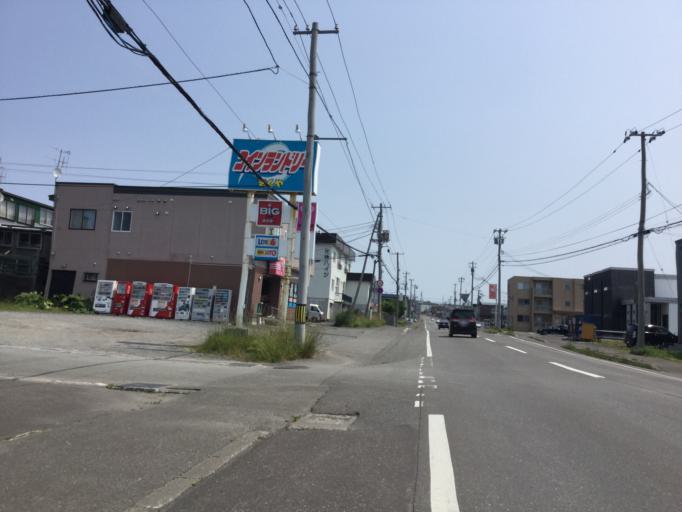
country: JP
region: Hokkaido
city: Wakkanai
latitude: 45.3864
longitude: 141.7113
